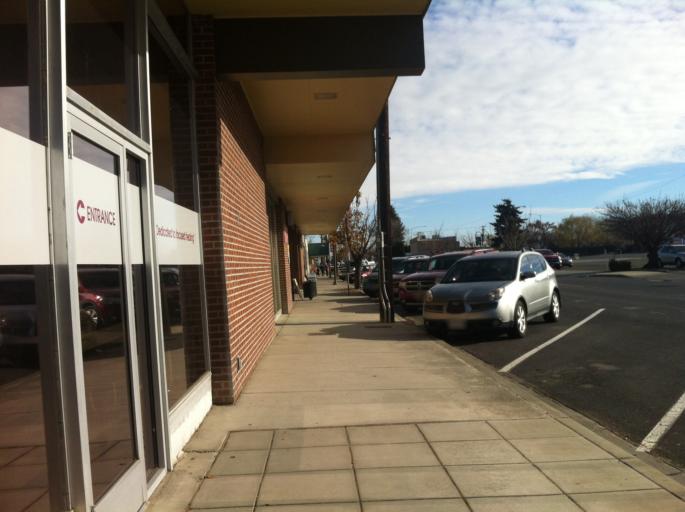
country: US
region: Washington
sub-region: Grant County
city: Quincy
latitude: 47.2340
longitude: -119.8530
